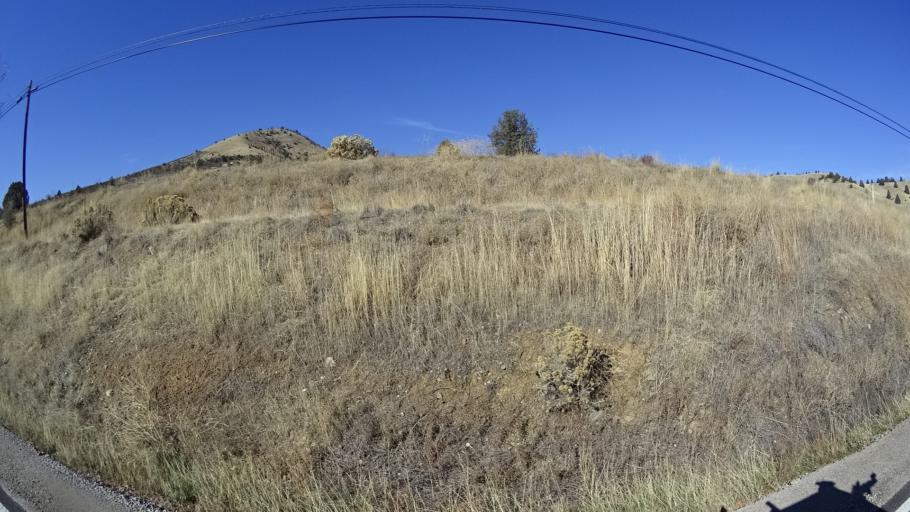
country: US
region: California
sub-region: Siskiyou County
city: Yreka
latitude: 41.7771
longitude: -122.5979
